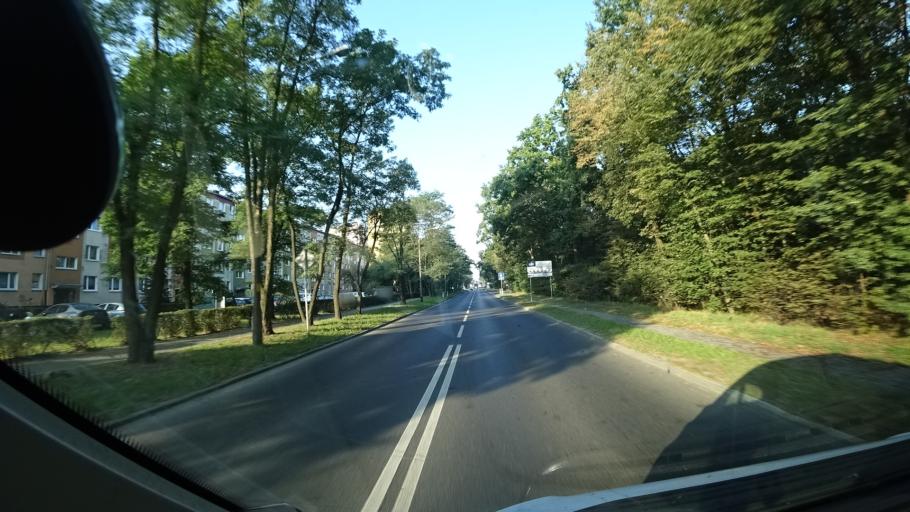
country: PL
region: Opole Voivodeship
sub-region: Powiat kedzierzynsko-kozielski
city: Kedzierzyn-Kozle
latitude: 50.3511
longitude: 18.2307
